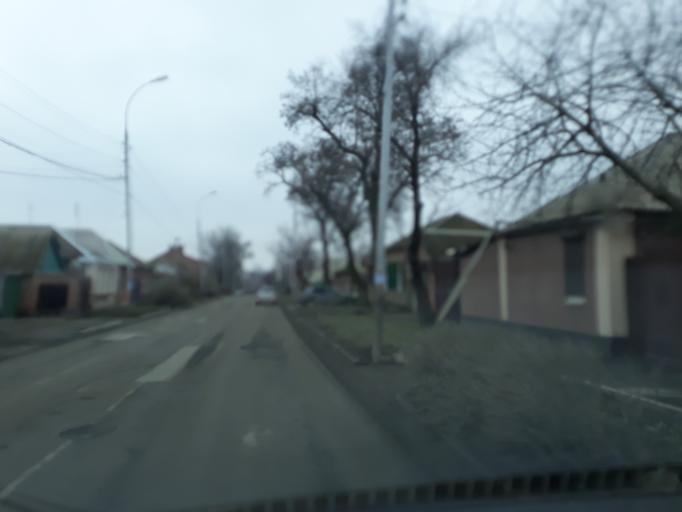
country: RU
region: Rostov
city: Taganrog
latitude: 47.2347
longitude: 38.9262
